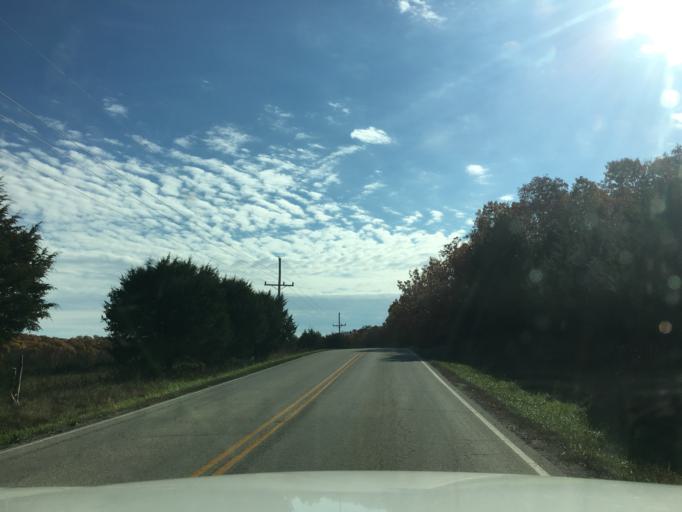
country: US
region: Missouri
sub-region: Maries County
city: Belle
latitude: 38.3336
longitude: -91.7626
